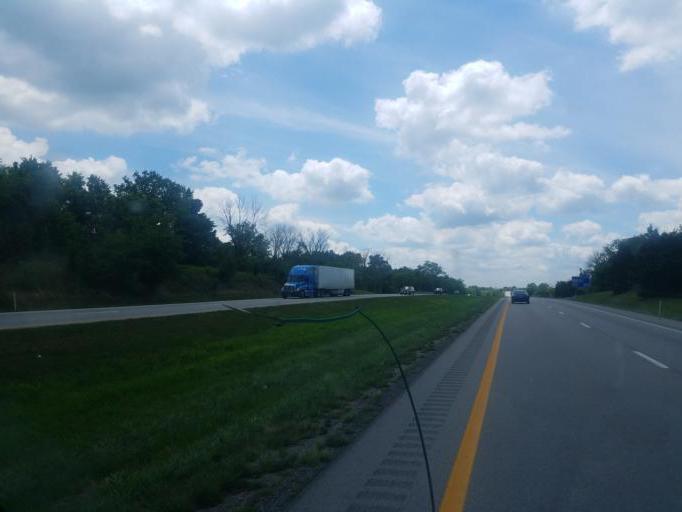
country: US
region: Kentucky
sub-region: Trimble County
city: Providence
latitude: 38.5285
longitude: -85.2277
